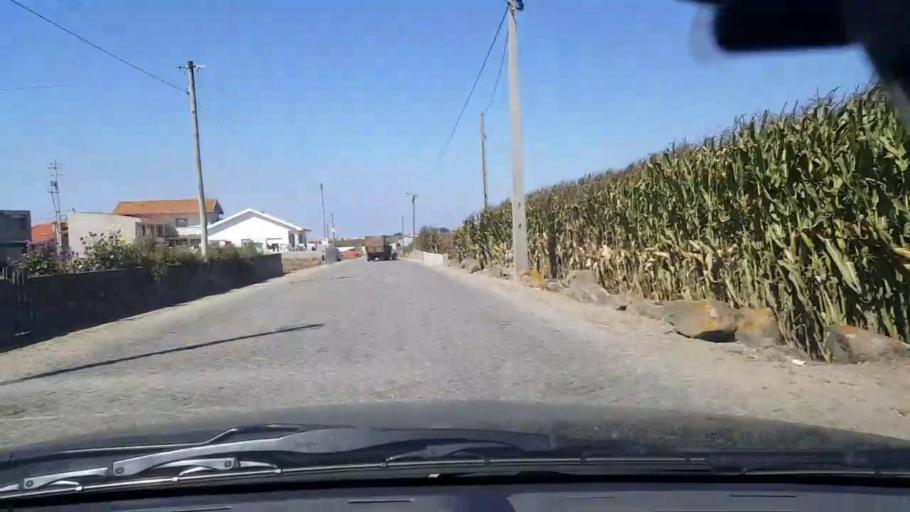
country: PT
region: Porto
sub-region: Matosinhos
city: Lavra
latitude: 41.2848
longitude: -8.7243
